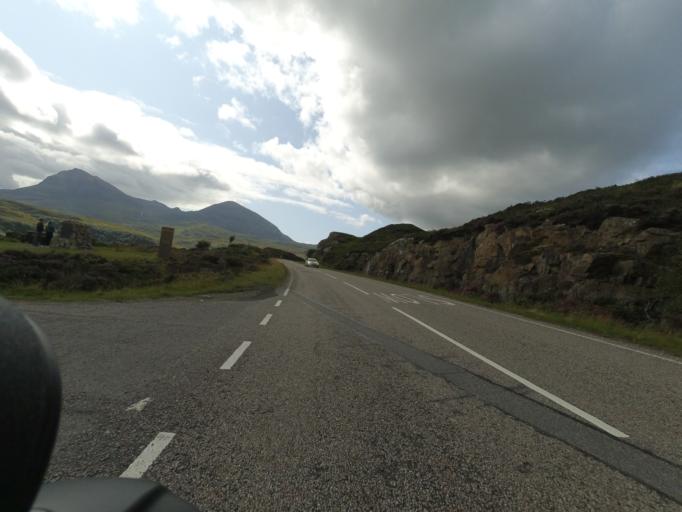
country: GB
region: Scotland
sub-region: Highland
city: Ullapool
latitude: 58.2576
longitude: -5.0275
